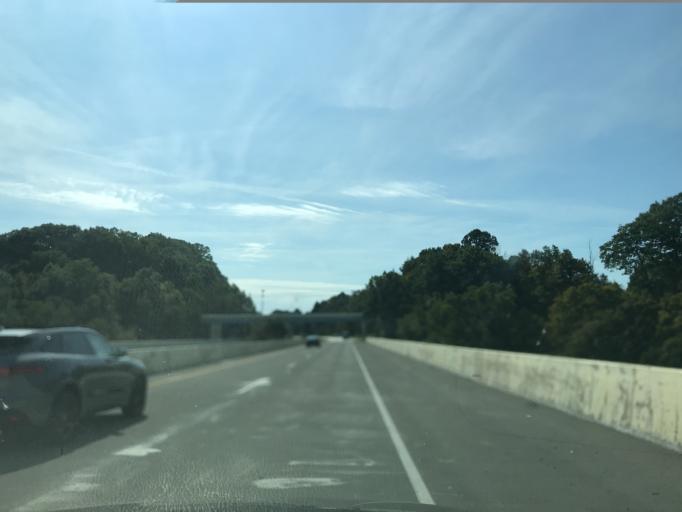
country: US
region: Ohio
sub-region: Ashtabula County
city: Edgewood
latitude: 41.8534
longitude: -80.7669
